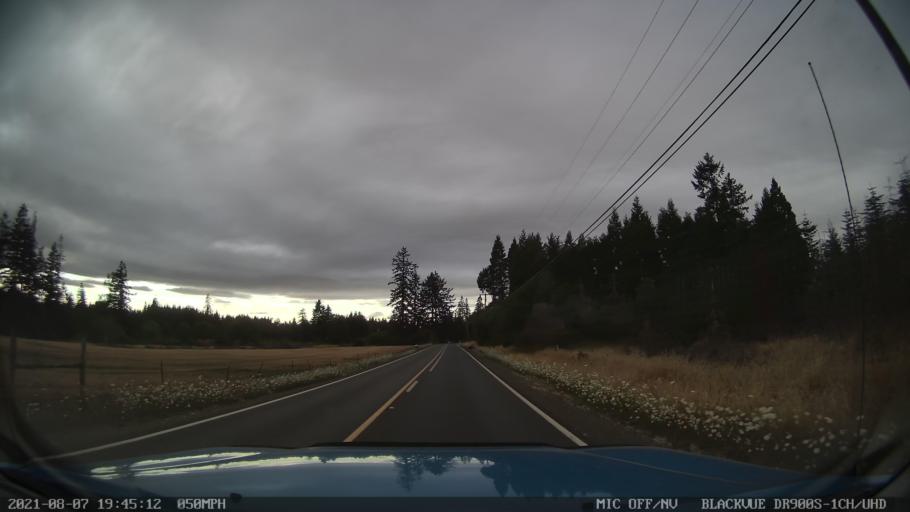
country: US
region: Oregon
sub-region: Marion County
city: Silverton
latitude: 44.9460
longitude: -122.6930
